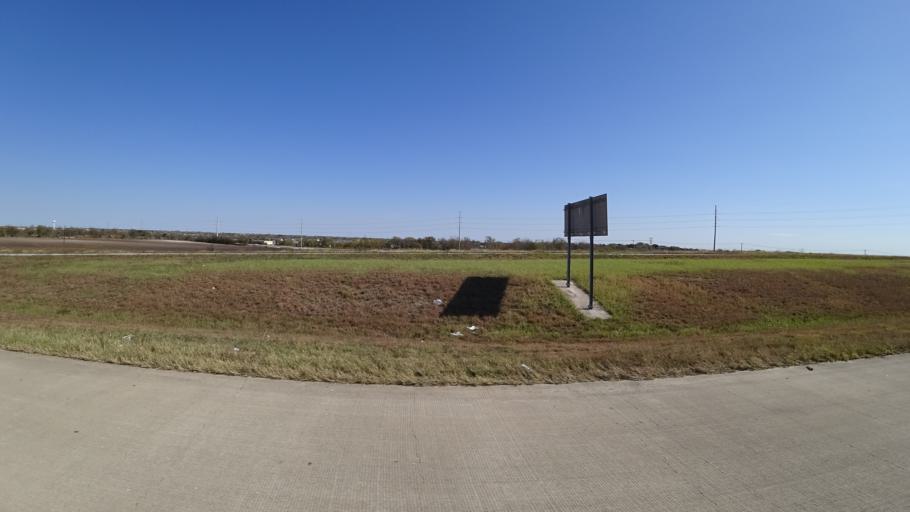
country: US
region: Texas
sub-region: Williamson County
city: Hutto
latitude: 30.5171
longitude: -97.5751
